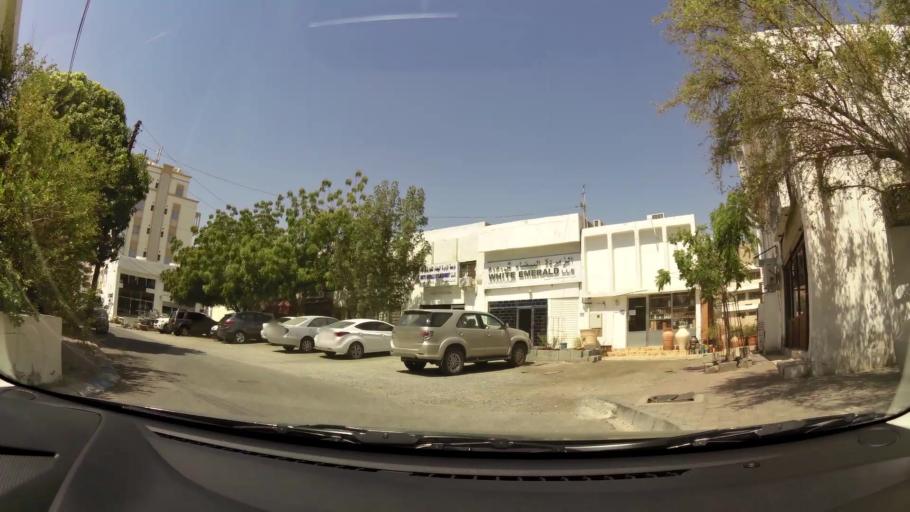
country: OM
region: Muhafazat Masqat
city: Muscat
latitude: 23.6016
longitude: 58.5394
